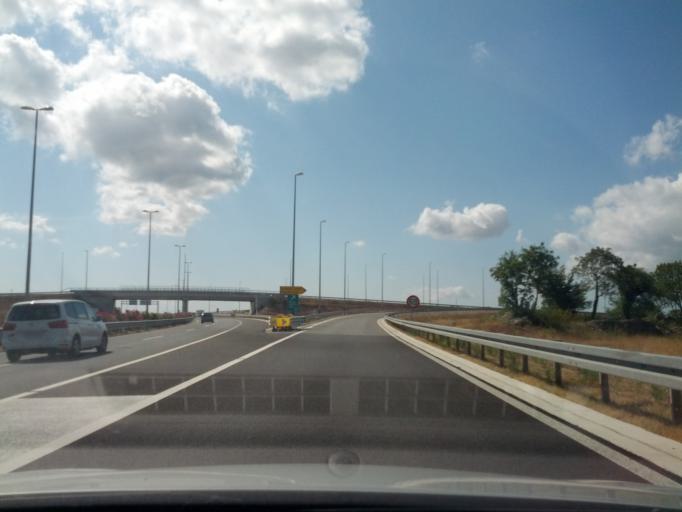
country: HR
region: Istarska
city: Vodnjan
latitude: 44.9880
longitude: 13.8444
